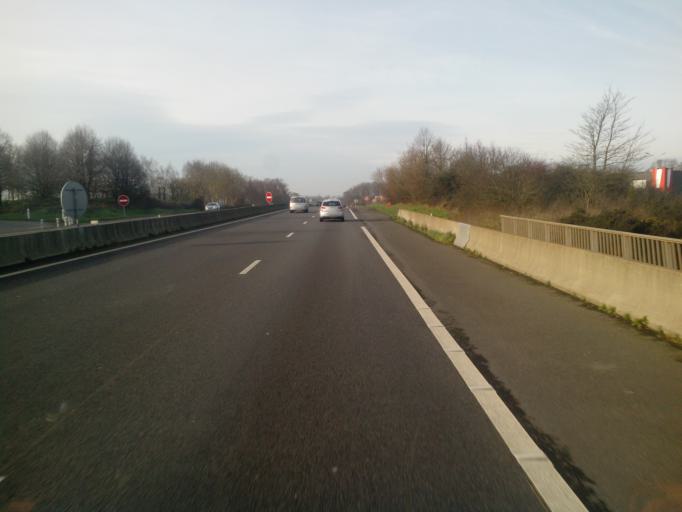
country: FR
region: Brittany
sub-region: Departement d'Ille-et-Vilaine
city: Pace
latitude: 48.1385
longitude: -1.7708
